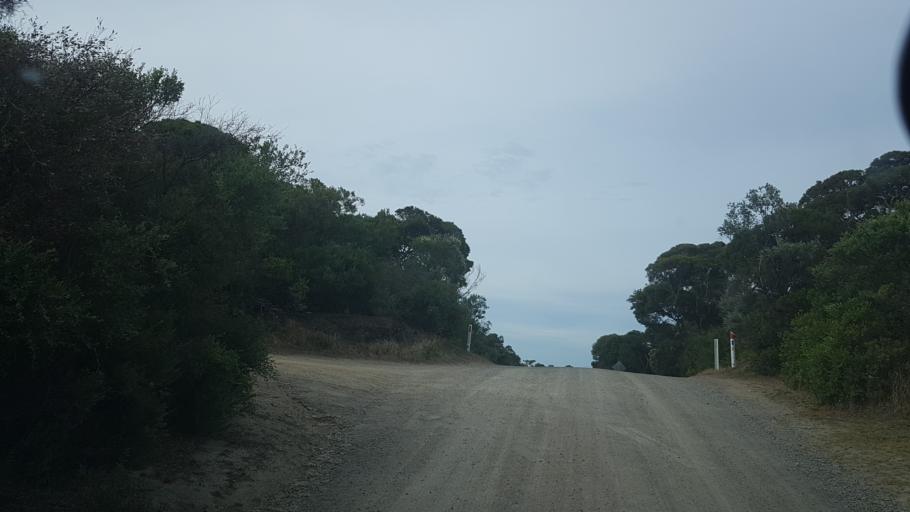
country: AU
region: Victoria
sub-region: Mornington Peninsula
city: Sorrento
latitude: -38.3328
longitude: 144.7159
